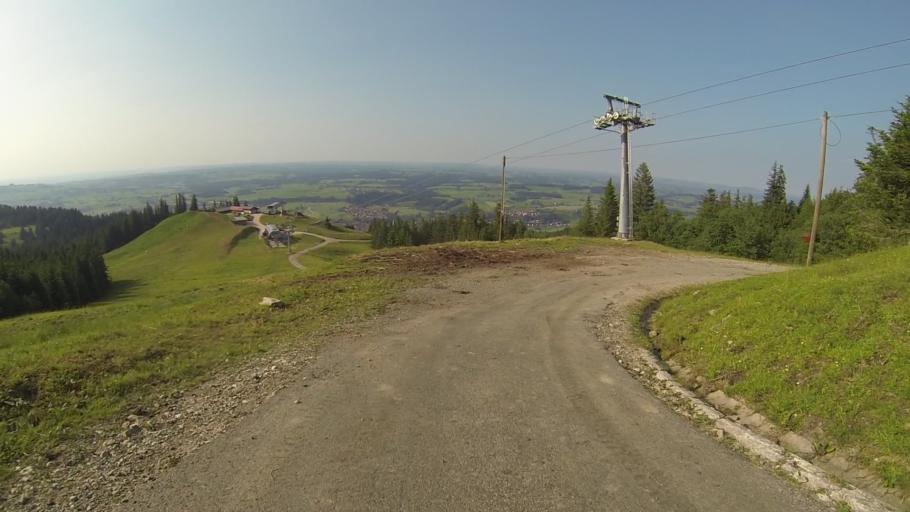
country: DE
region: Bavaria
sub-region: Swabia
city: Nesselwang
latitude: 47.6035
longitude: 10.4985
